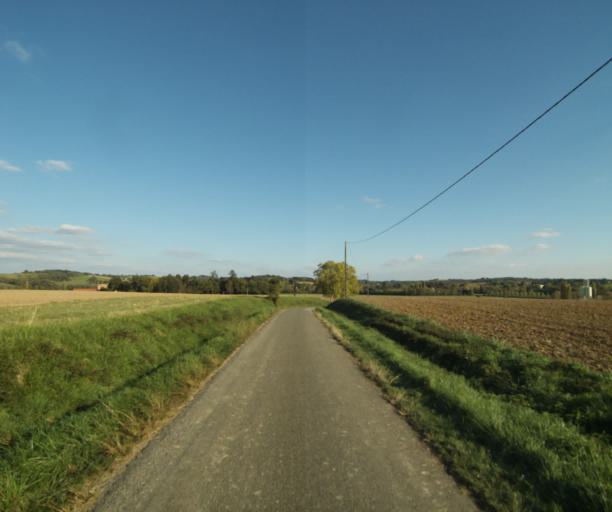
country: FR
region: Midi-Pyrenees
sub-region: Departement du Gers
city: Eauze
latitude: 43.7716
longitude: 0.1565
